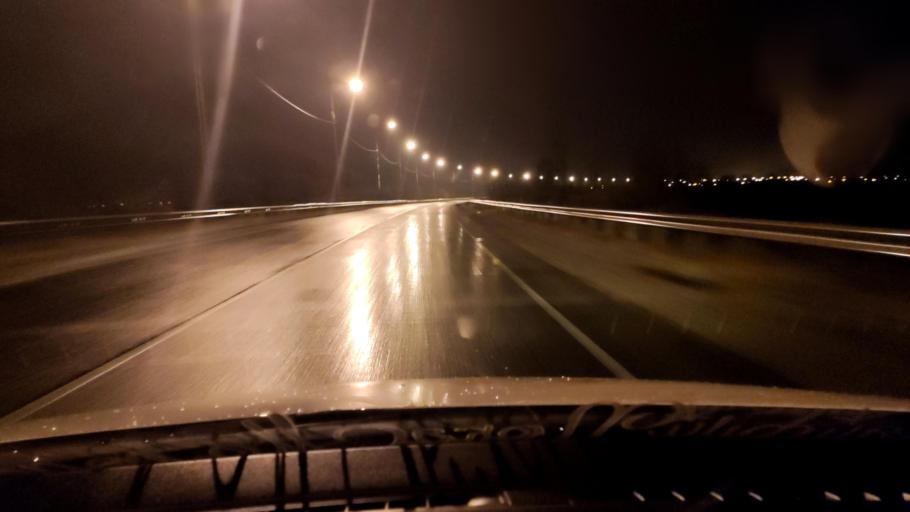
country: RU
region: Voronezj
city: Pridonskoy
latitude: 51.7194
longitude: 39.0721
